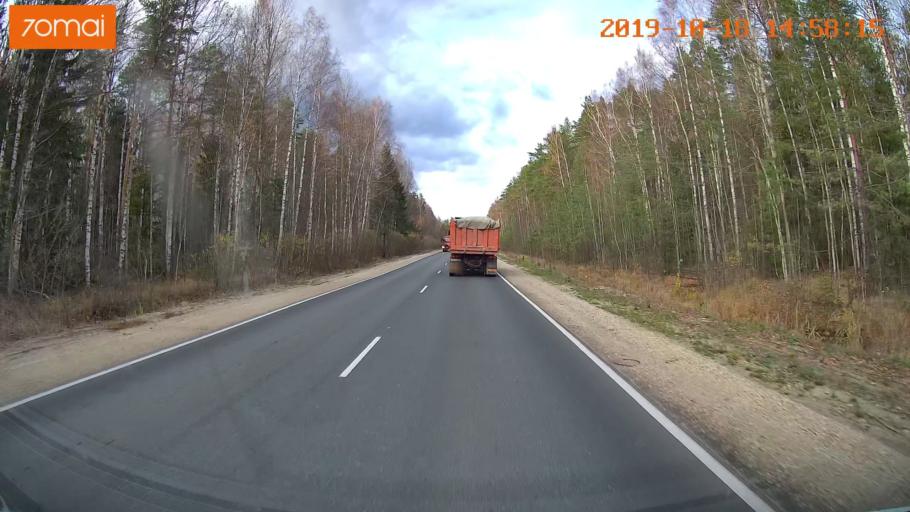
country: RU
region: Vladimir
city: Kurlovo
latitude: 55.4885
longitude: 40.5779
